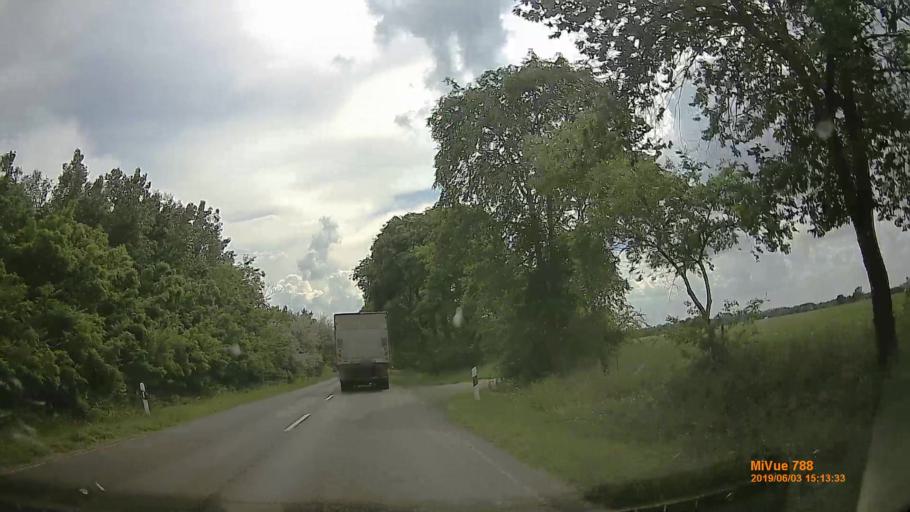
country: HU
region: Bacs-Kiskun
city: Orgovany
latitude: 46.7405
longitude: 19.5698
